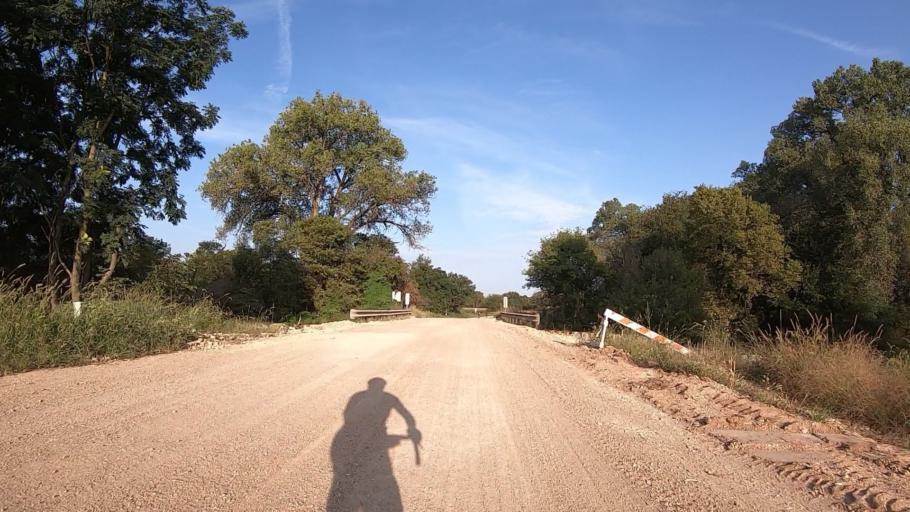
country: US
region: Kansas
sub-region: Marshall County
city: Blue Rapids
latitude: 39.7202
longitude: -96.7682
